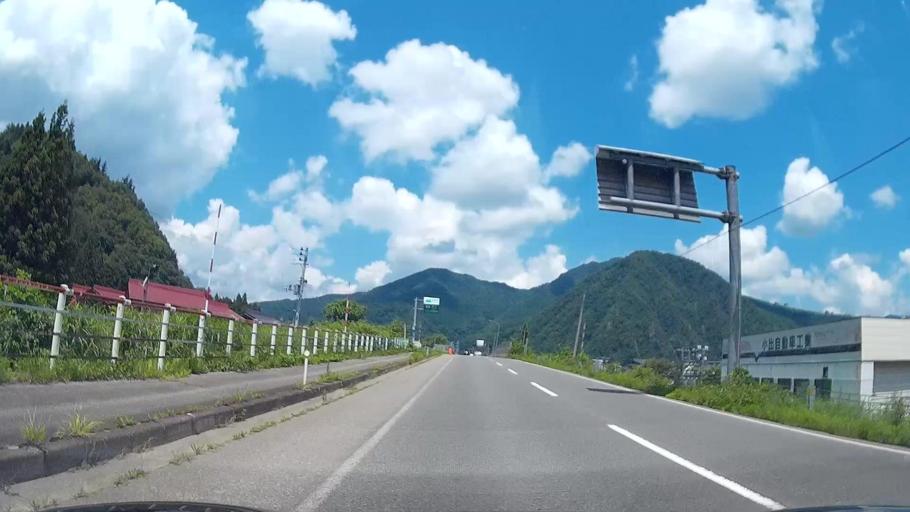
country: JP
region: Niigata
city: Shiozawa
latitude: 36.9263
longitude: 138.8239
